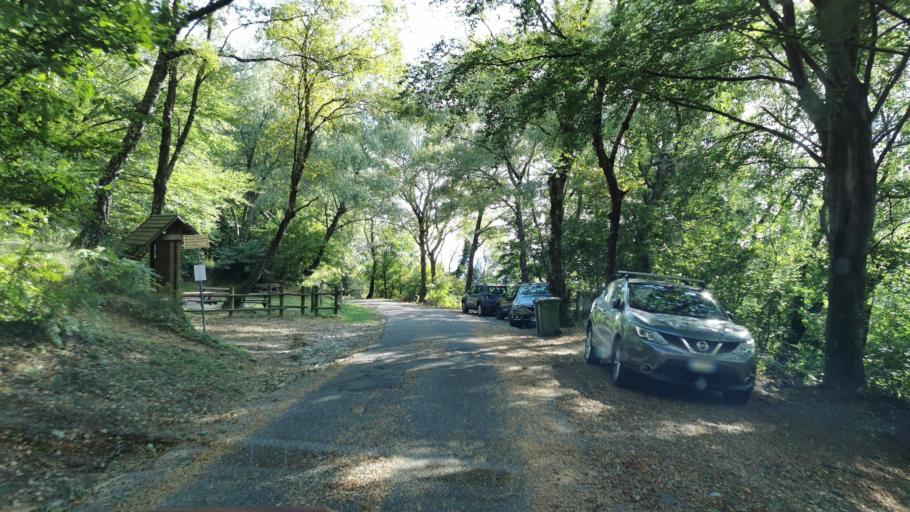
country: IT
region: Lombardy
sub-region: Provincia di Como
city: Cernobbio
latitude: 45.8630
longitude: 9.0768
